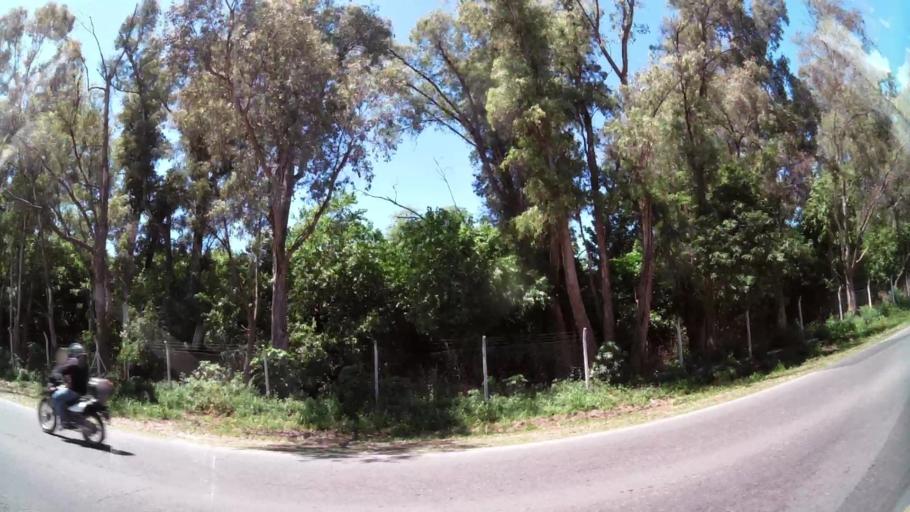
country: AR
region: Buenos Aires
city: Hurlingham
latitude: -34.5219
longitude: -58.6769
